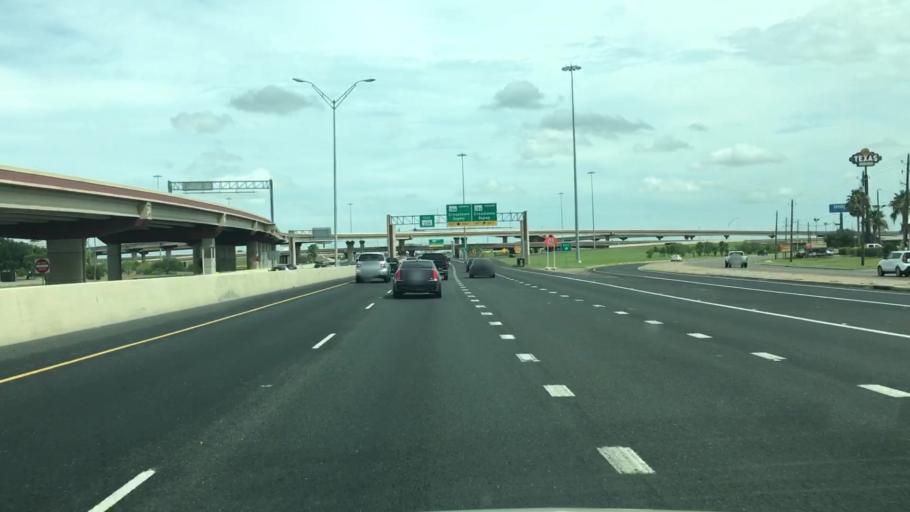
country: US
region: Texas
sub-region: Nueces County
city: Corpus Christi
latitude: 27.7395
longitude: -97.4354
